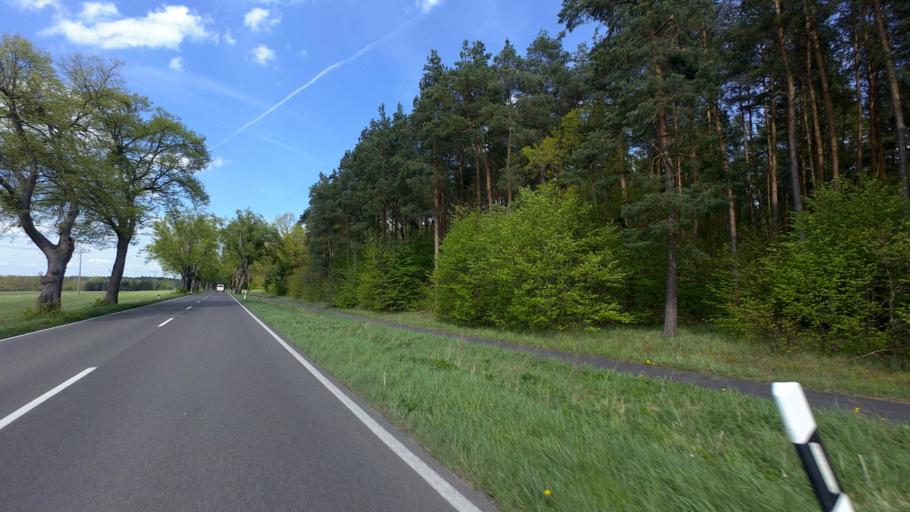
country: DE
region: Brandenburg
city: Milmersdorf
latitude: 53.0667
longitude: 13.6235
